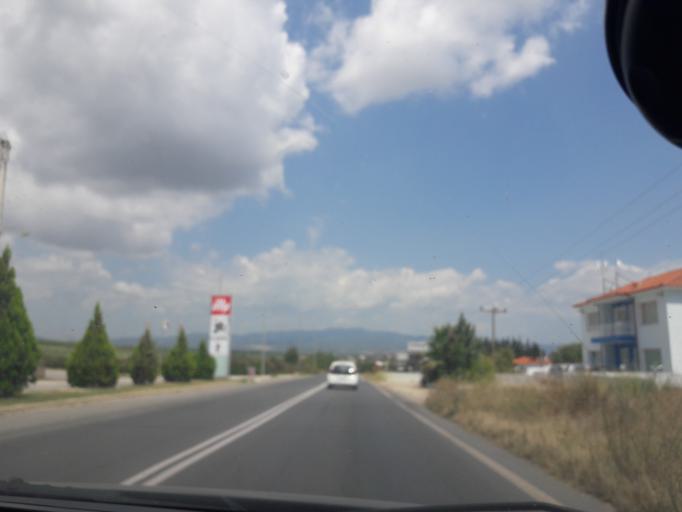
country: GR
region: Central Macedonia
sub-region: Nomos Chalkidikis
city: Olynthos
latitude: 40.2581
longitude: 23.3272
